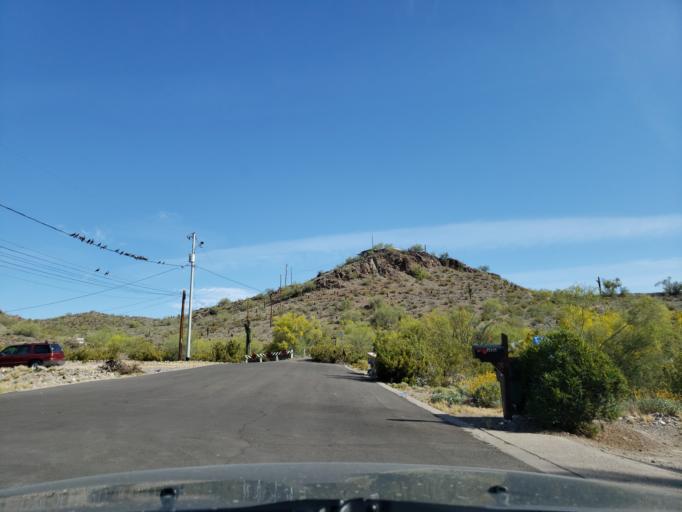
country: US
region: Arizona
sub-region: Maricopa County
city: Paradise Valley
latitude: 33.5926
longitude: -112.0477
